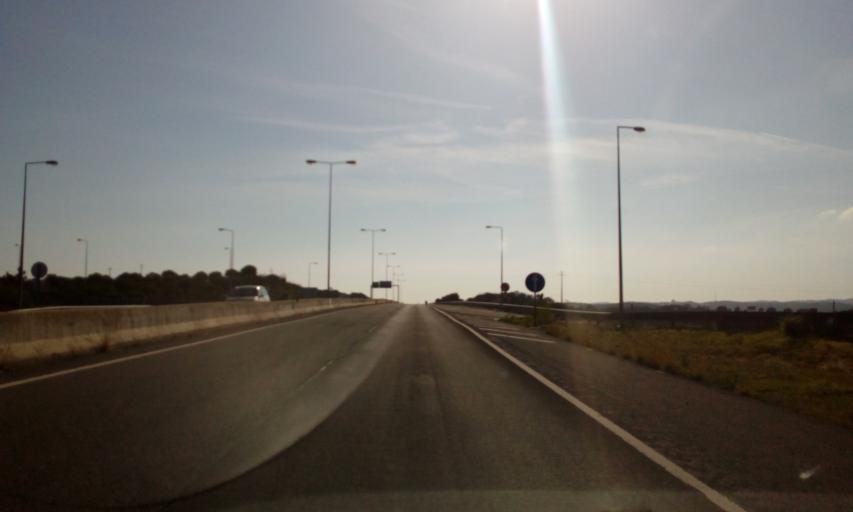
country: PT
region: Faro
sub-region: Castro Marim
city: Castro Marim
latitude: 37.2929
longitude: -7.4874
